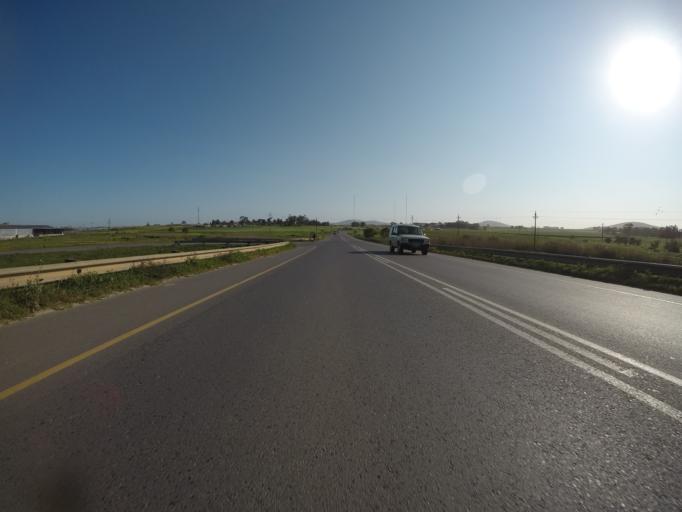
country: ZA
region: Western Cape
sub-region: City of Cape Town
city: Kraaifontein
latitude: -33.7837
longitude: 18.7097
